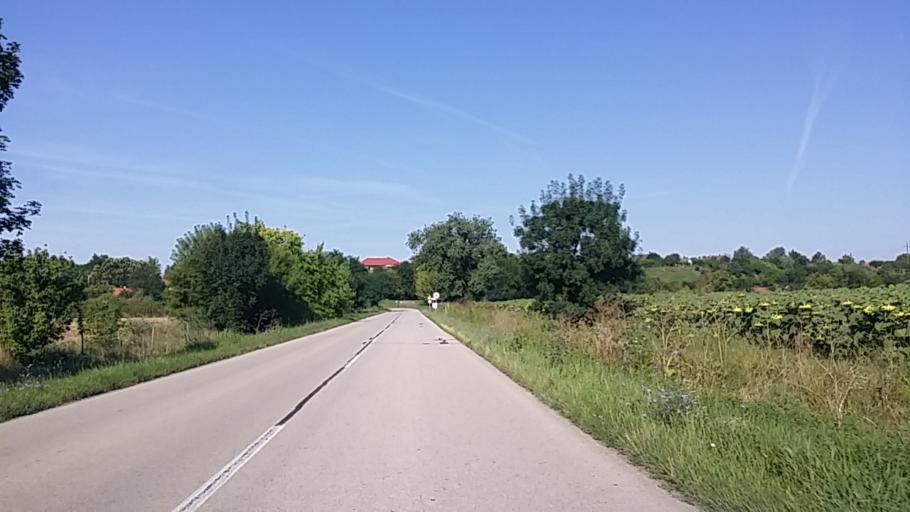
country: HU
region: Fejer
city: Ivancsa
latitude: 47.1405
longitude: 18.8426
